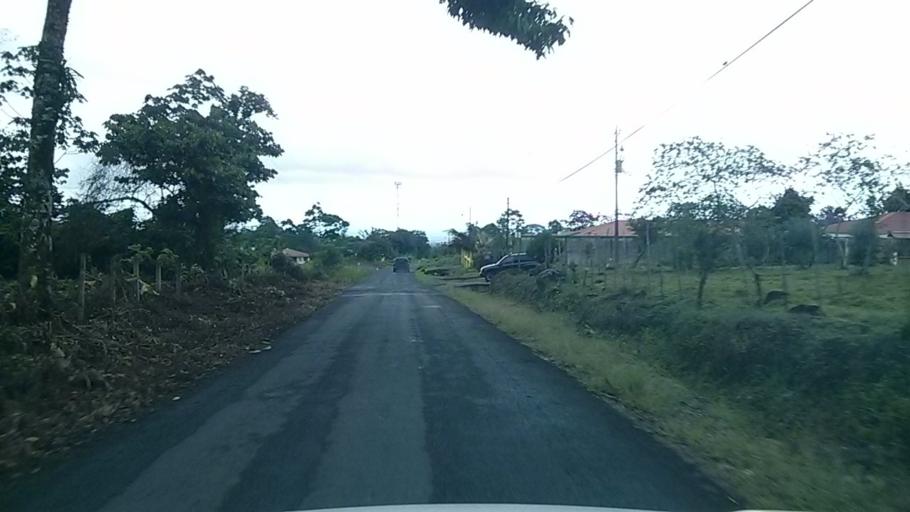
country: CR
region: Limon
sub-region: Canton de Pococi
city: Guapiles
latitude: 10.1789
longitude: -83.7835
